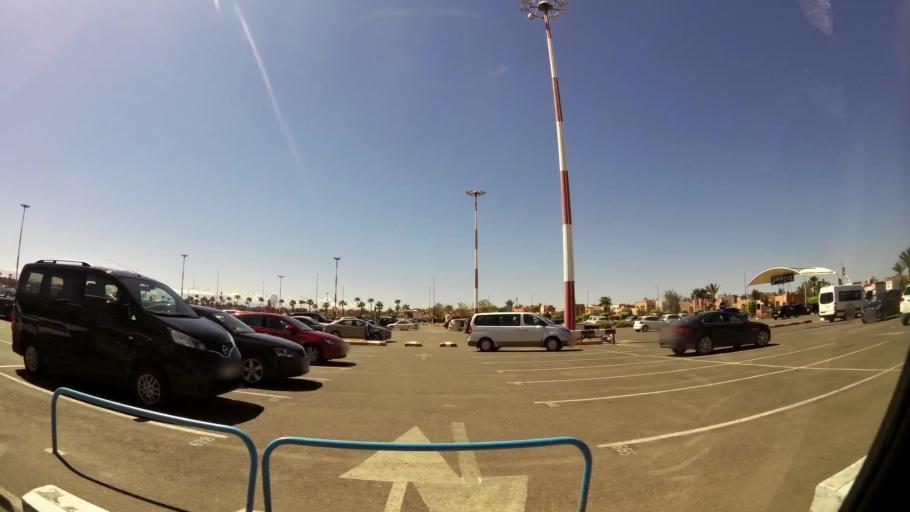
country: MA
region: Marrakech-Tensift-Al Haouz
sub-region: Marrakech
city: Marrakesh
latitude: 31.6009
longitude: -8.0276
